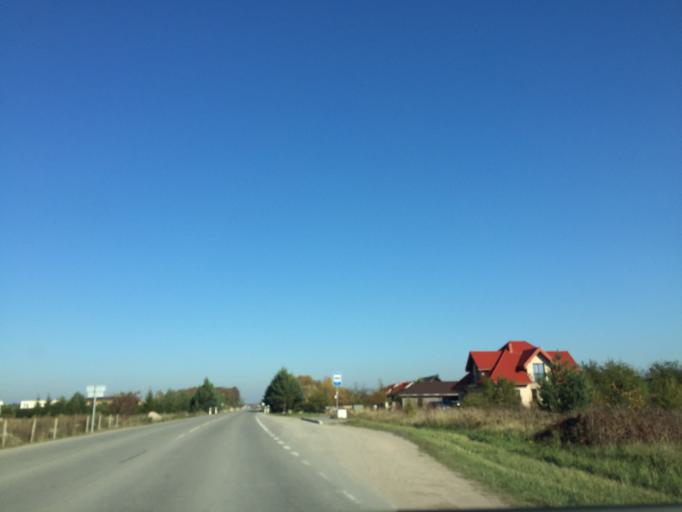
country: LT
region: Klaipedos apskritis
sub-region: Klaipeda
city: Klaipeda
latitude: 55.7558
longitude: 21.1928
